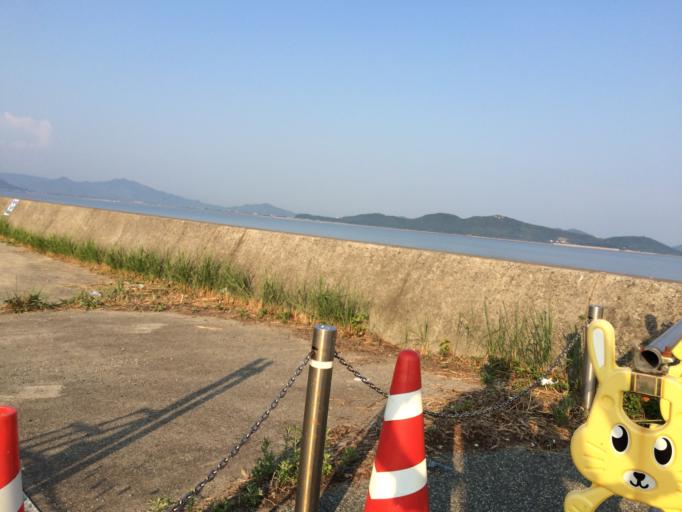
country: JP
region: Yamaguchi
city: Ogori-shimogo
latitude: 34.0072
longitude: 131.3772
